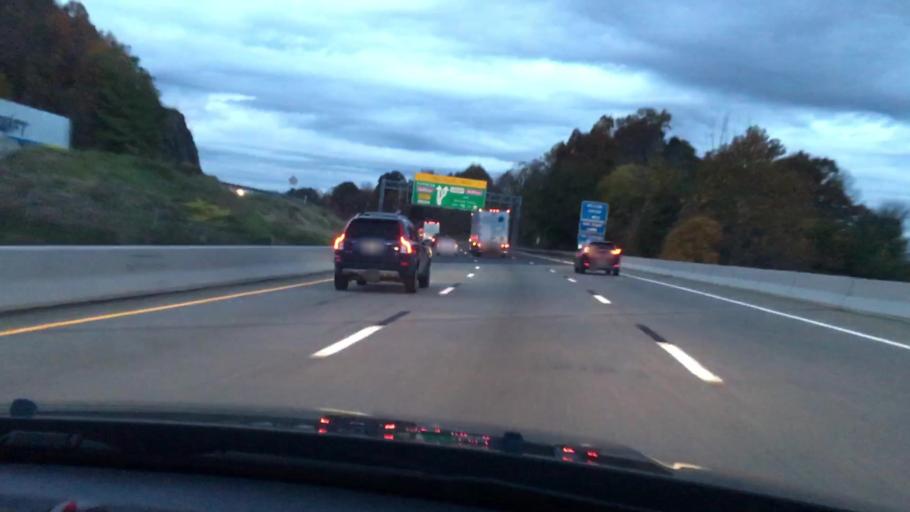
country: US
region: New Jersey
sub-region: Warren County
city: Phillipsburg
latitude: 40.6755
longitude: -75.1809
